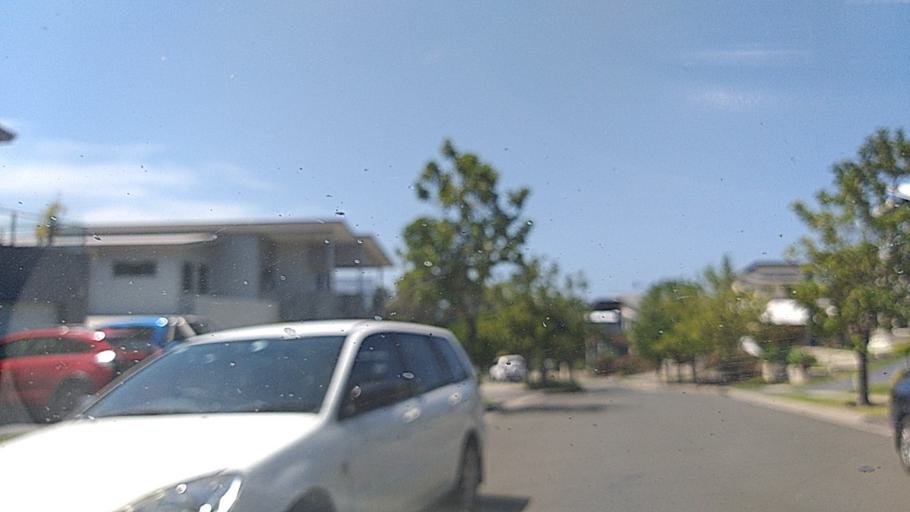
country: AU
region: New South Wales
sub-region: Wollongong
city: Bulli
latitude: -34.3287
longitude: 150.9177
